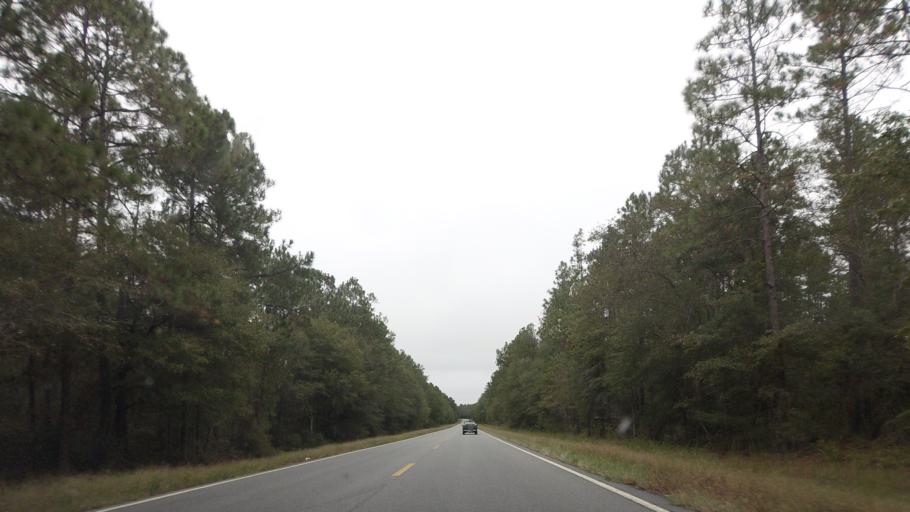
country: US
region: Georgia
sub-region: Berrien County
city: Enigma
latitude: 31.4121
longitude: -83.2425
